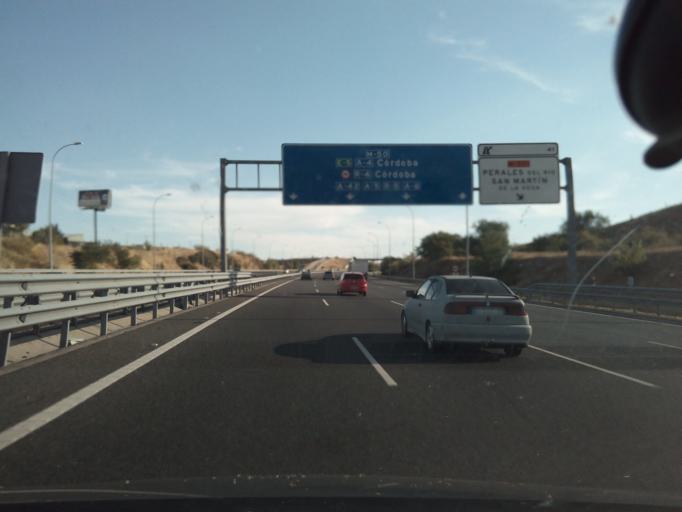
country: ES
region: Madrid
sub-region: Provincia de Madrid
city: Villaverde
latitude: 40.3127
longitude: -3.6497
